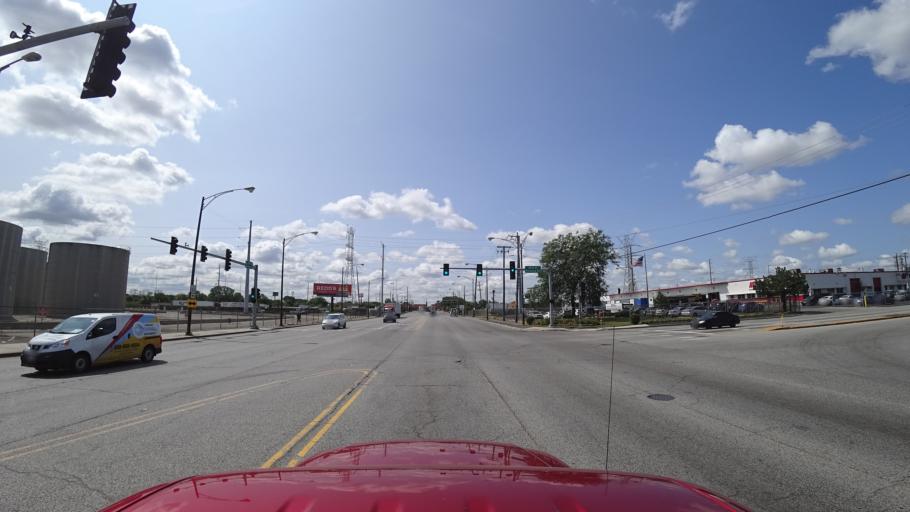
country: US
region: Illinois
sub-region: Cook County
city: Cicero
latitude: 41.8223
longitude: -87.7436
